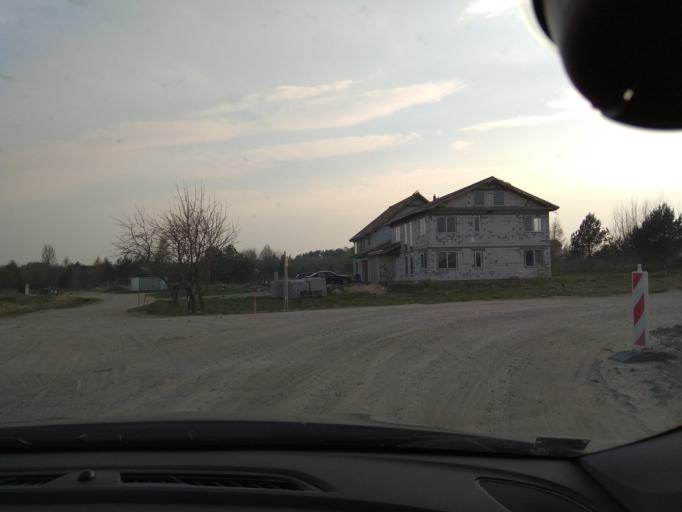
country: LT
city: Baltoji Voke
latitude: 54.5924
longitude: 25.1588
